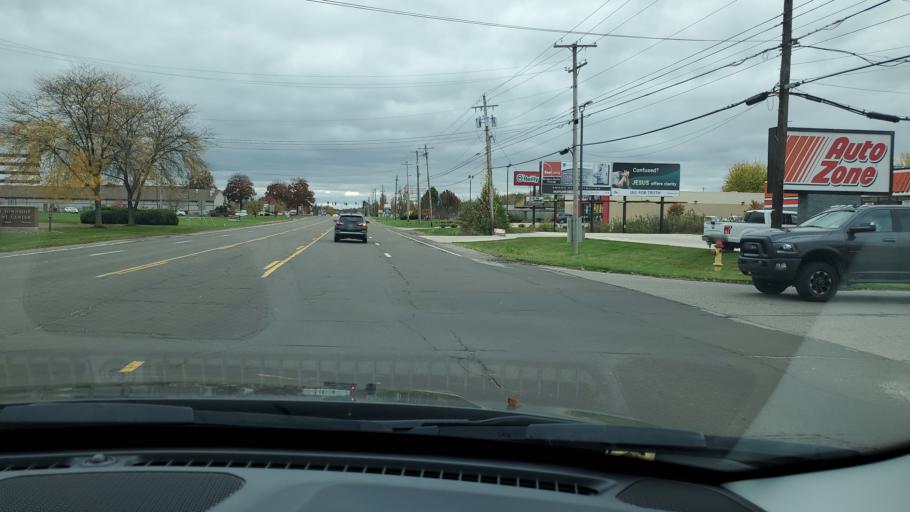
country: US
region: Ohio
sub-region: Mahoning County
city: Boardman
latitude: 40.9983
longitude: -80.6628
